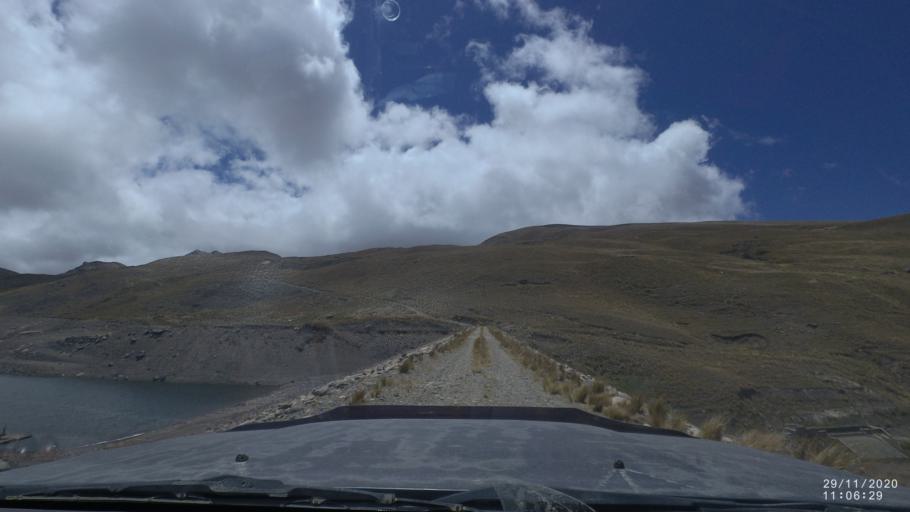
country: BO
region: Cochabamba
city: Cochabamba
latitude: -17.1855
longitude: -66.2094
